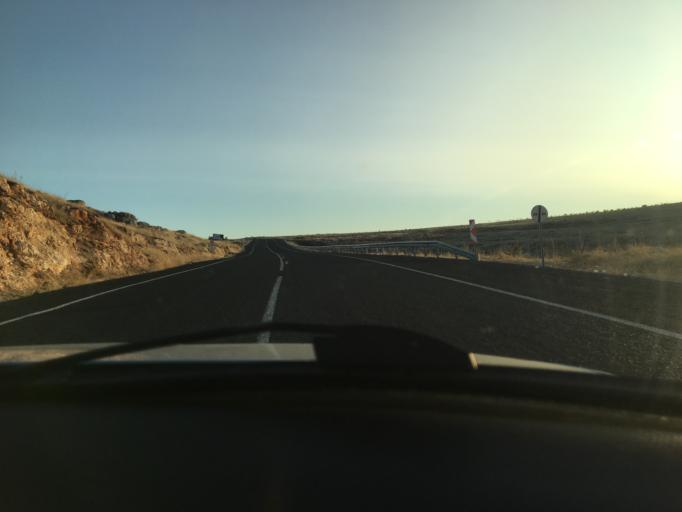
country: TR
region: Sanliurfa
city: Bogurtlen
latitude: 37.1828
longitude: 37.9757
